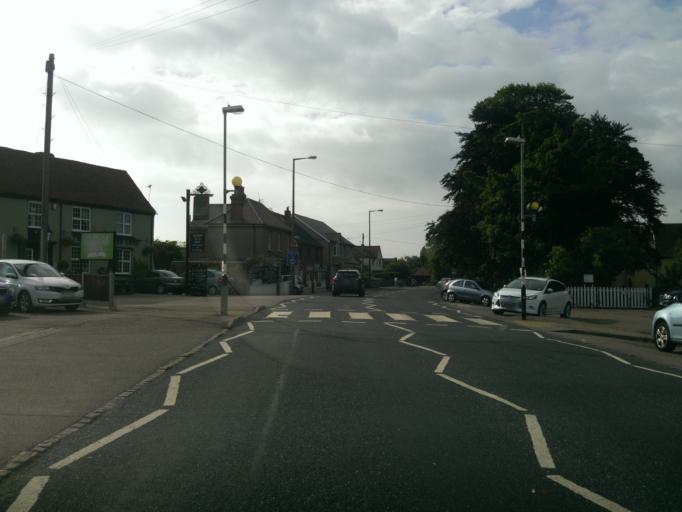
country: GB
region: England
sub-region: Essex
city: Little Clacton
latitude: 51.8269
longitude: 1.1422
